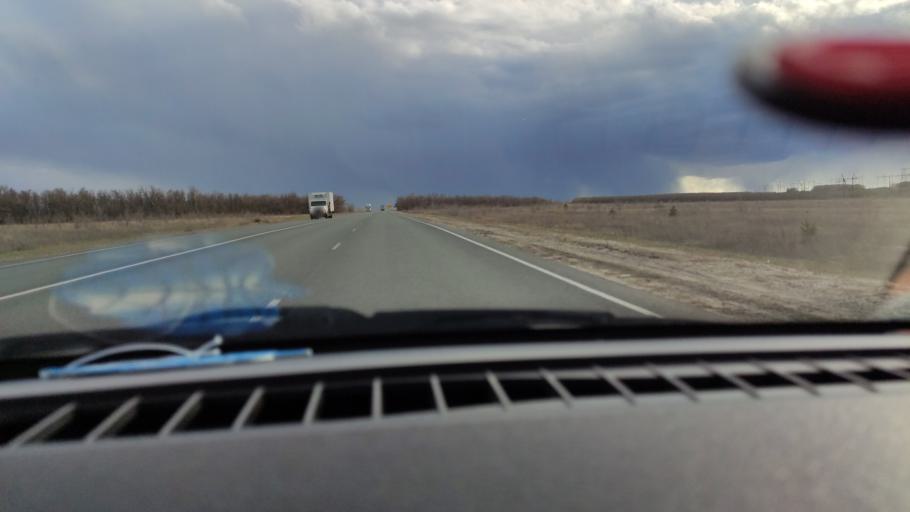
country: RU
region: Saratov
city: Sinodskoye
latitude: 51.9109
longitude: 46.5525
